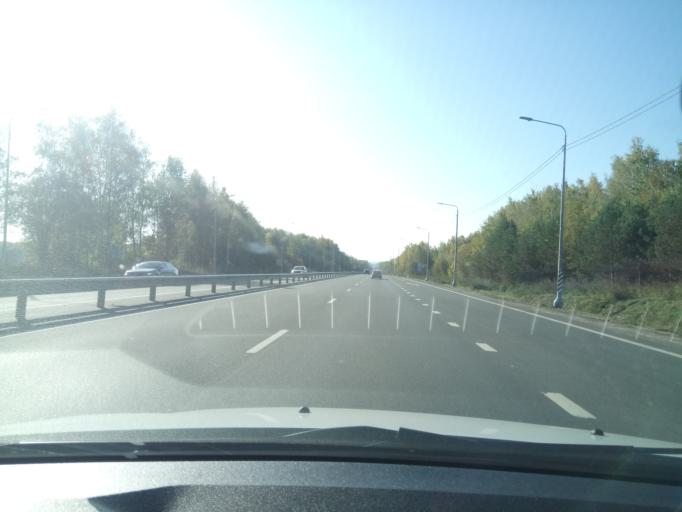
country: RU
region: Nizjnij Novgorod
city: Burevestnik
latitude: 56.0343
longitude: 43.9612
